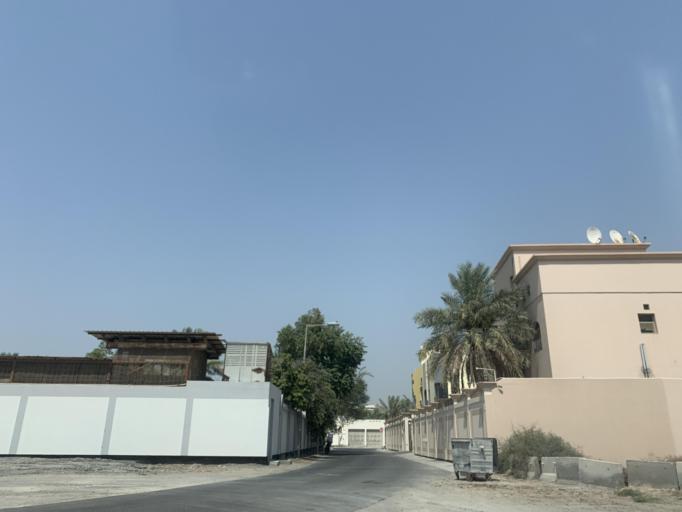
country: BH
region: Manama
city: Jidd Hafs
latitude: 26.2007
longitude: 50.5234
